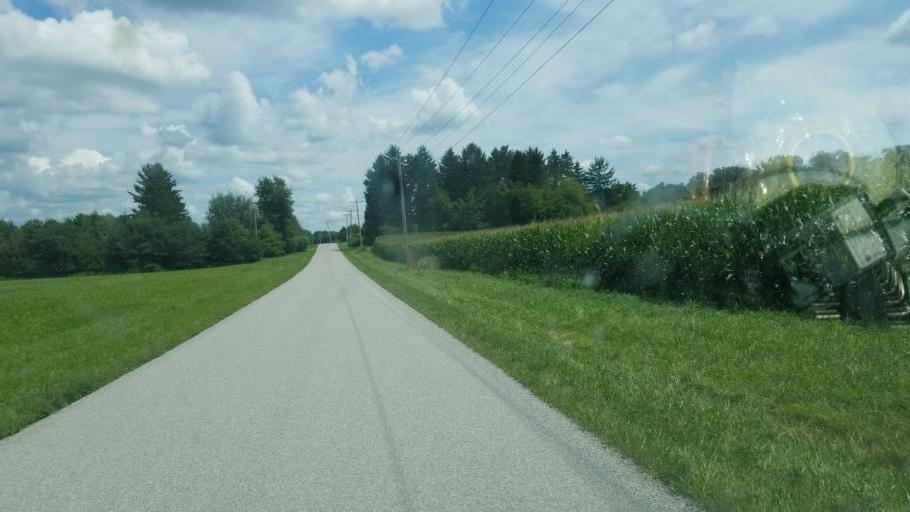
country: US
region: Ohio
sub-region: Knox County
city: Centerburg
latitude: 40.3730
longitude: -82.7099
